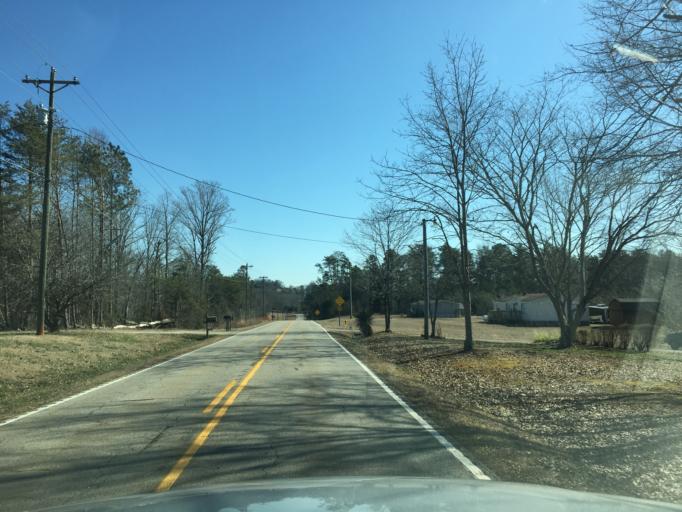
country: US
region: South Carolina
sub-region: Pickens County
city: Liberty
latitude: 34.8036
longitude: -82.7531
